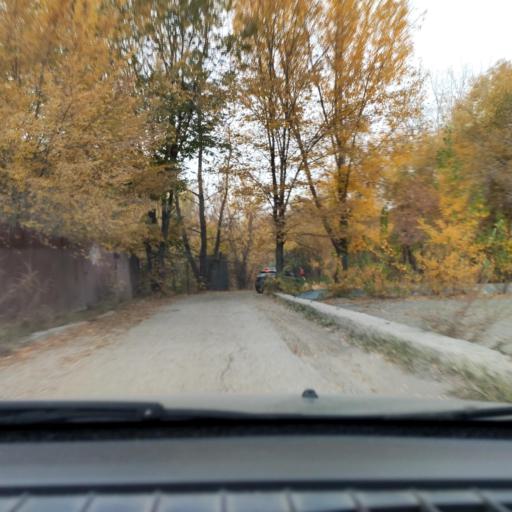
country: RU
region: Samara
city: Tol'yatti
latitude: 53.4990
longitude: 49.2618
